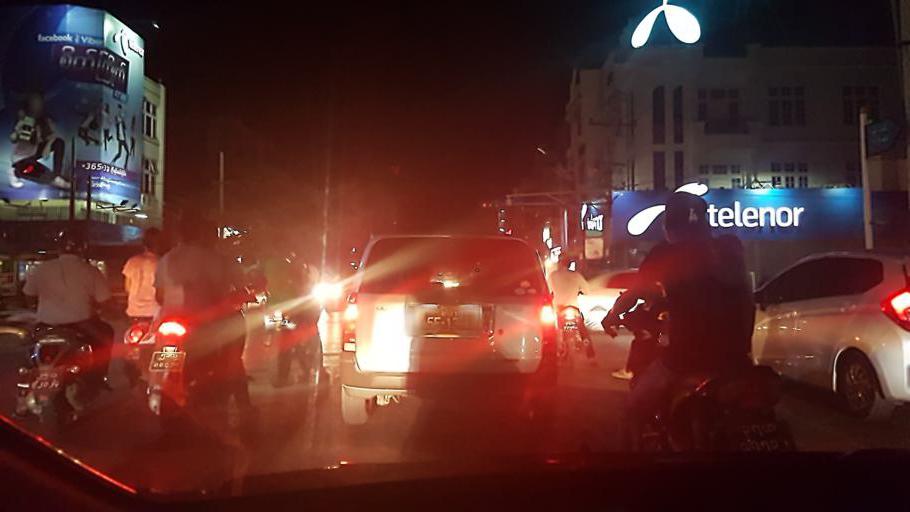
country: MM
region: Mandalay
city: Mandalay
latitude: 21.9762
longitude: 96.0956
